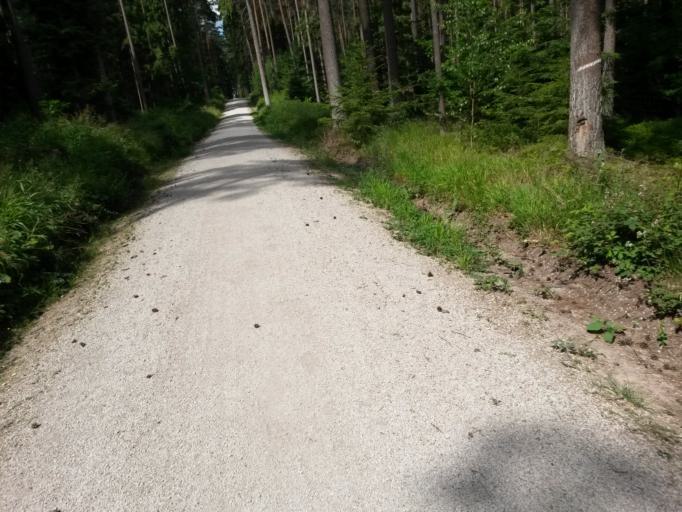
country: DE
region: Bavaria
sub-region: Regierungsbezirk Mittelfranken
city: Seukendorf
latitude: 49.4686
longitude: 10.8982
